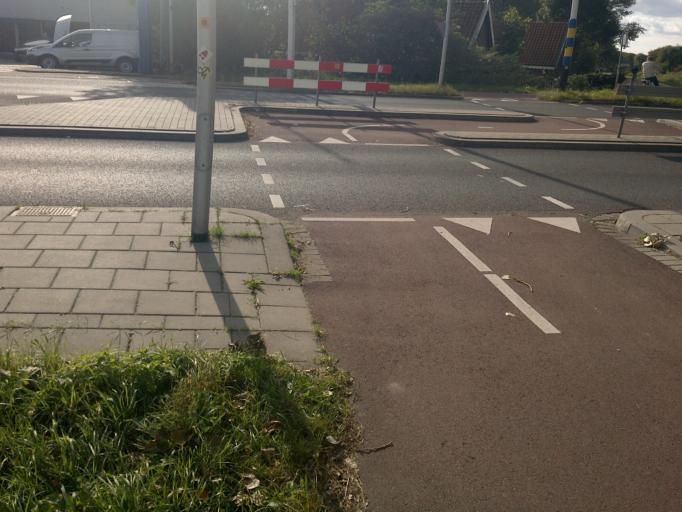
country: NL
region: South Holland
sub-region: Gemeente Zoetermeer
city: Zoetermeer
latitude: 52.0716
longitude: 4.4799
